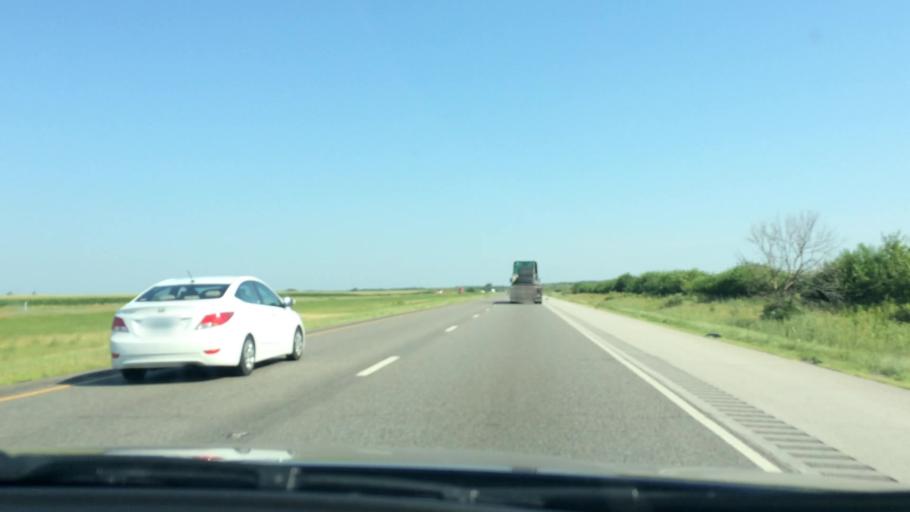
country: US
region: Indiana
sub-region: Jasper County
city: Rensselaer
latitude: 40.8808
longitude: -87.1969
